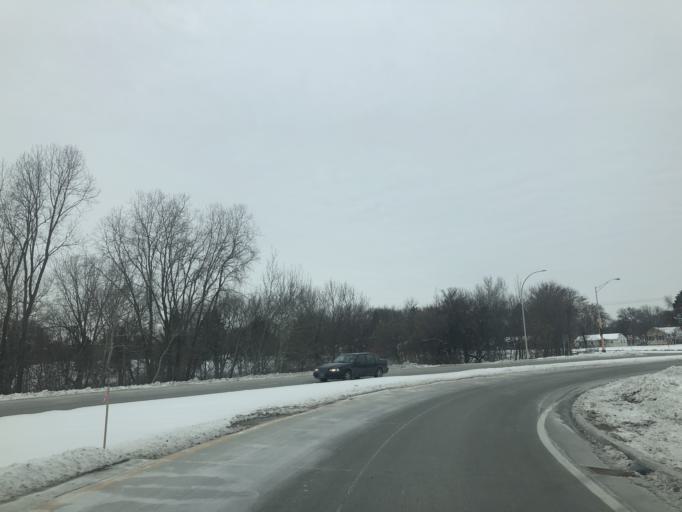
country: US
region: Minnesota
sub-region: Ramsey County
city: Mounds View
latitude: 45.1070
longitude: -93.1899
